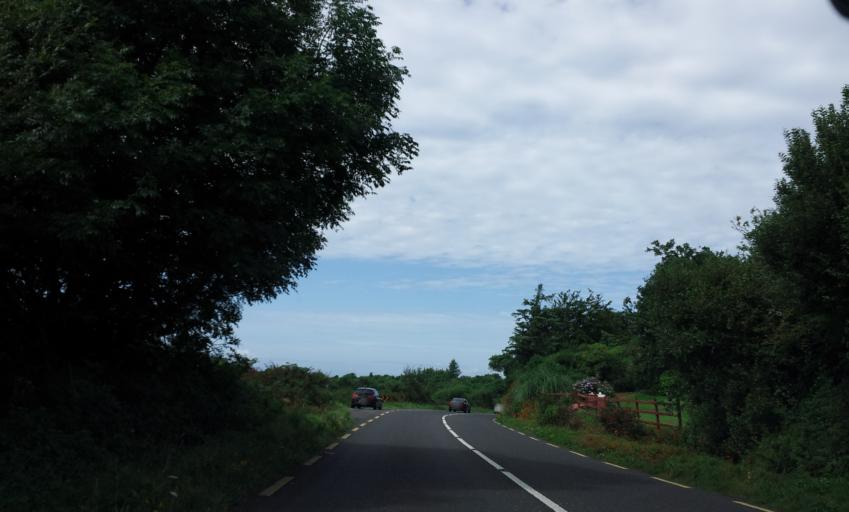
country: IE
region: Munster
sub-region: Ciarrai
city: Killorglin
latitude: 52.0702
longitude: -9.8902
